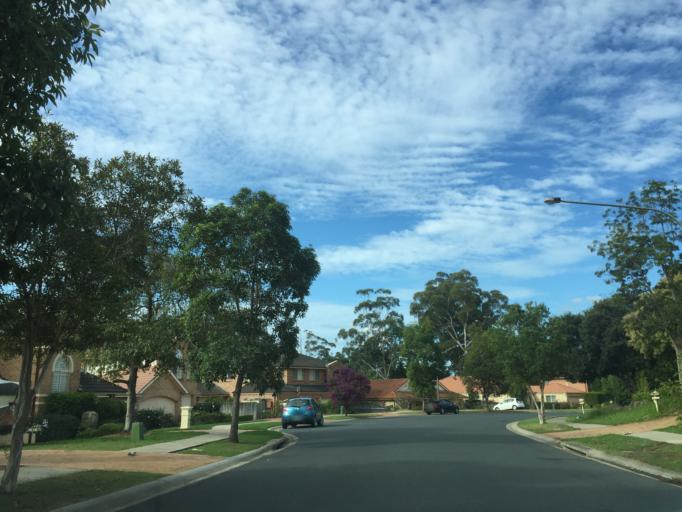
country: AU
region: New South Wales
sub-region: The Hills Shire
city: Beaumont Hills
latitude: -33.7045
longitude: 150.9633
